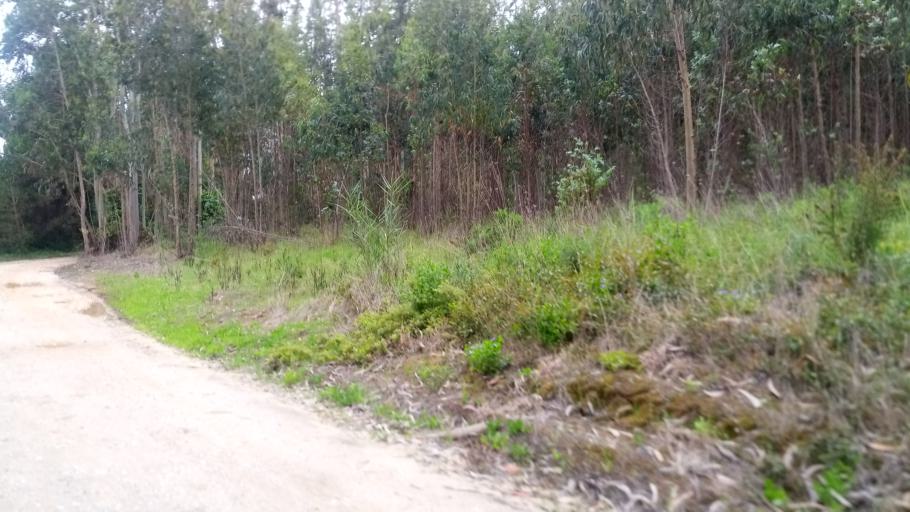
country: PT
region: Leiria
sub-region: Caldas da Rainha
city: Caldas da Rainha
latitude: 39.4490
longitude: -9.1847
